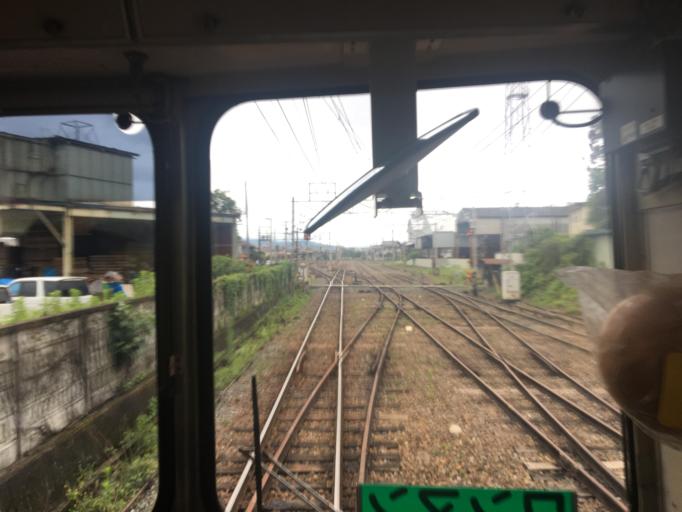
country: JP
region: Saitama
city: Chichibu
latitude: 35.9704
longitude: 139.0672
